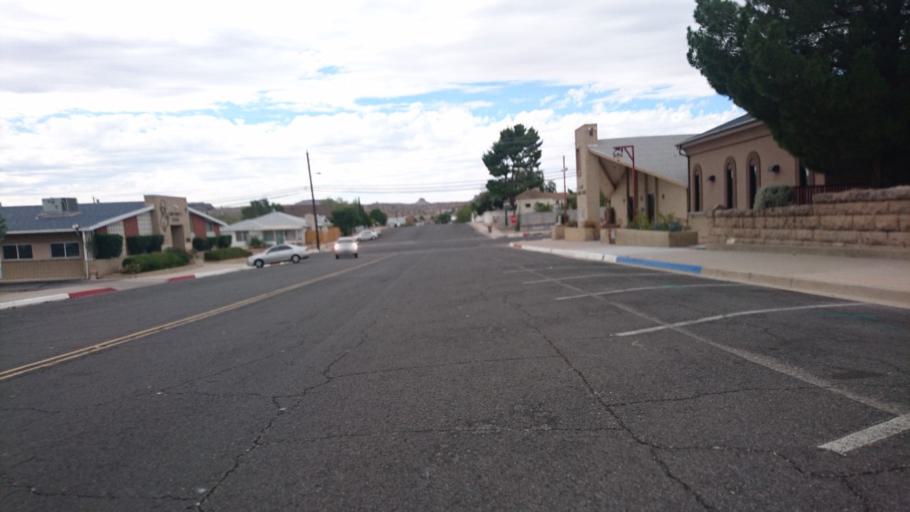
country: US
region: Arizona
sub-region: Mohave County
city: Kingman
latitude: 35.1918
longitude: -114.0535
